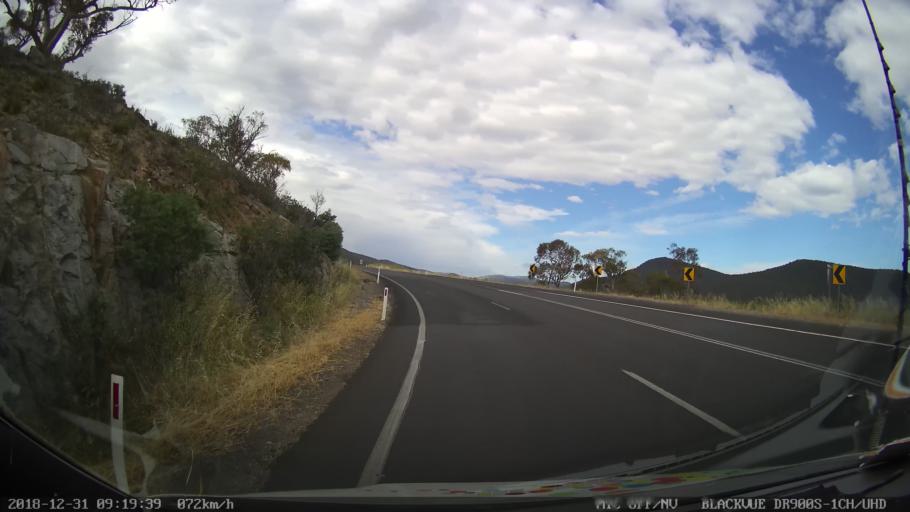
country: AU
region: New South Wales
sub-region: Snowy River
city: Jindabyne
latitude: -36.4164
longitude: 148.5834
